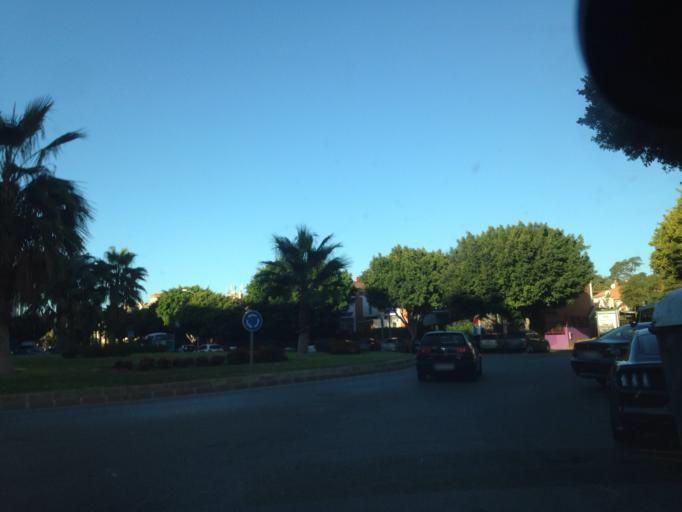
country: ES
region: Andalusia
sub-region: Provincia de Malaga
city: Malaga
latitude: 36.7216
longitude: -4.4795
